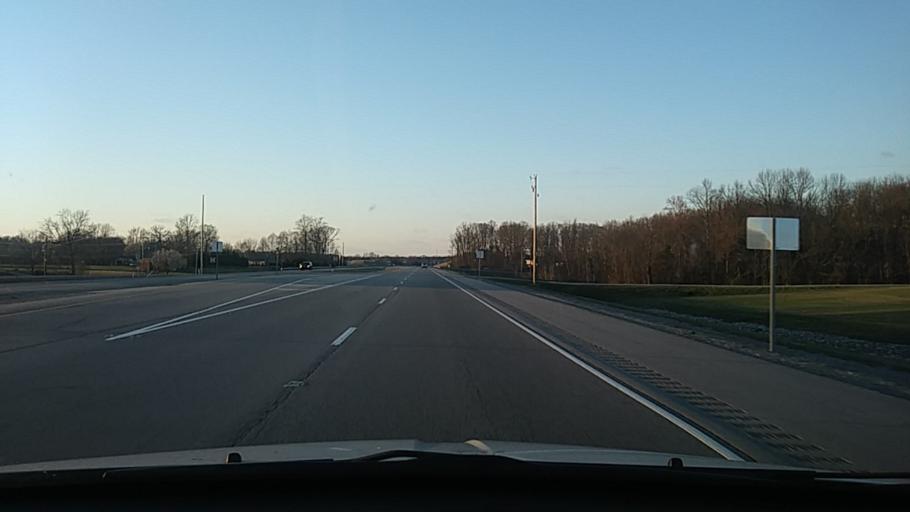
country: US
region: Tennessee
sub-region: Sumner County
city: Portland
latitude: 36.5135
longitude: -86.5060
